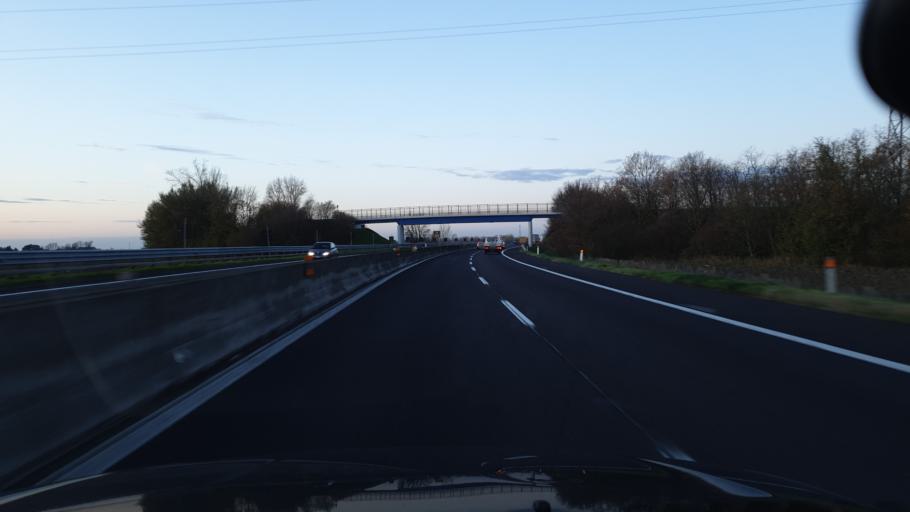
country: IT
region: Veneto
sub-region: Provincia di Rovigo
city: Fiesso Umbertiano
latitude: 44.9477
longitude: 11.6349
